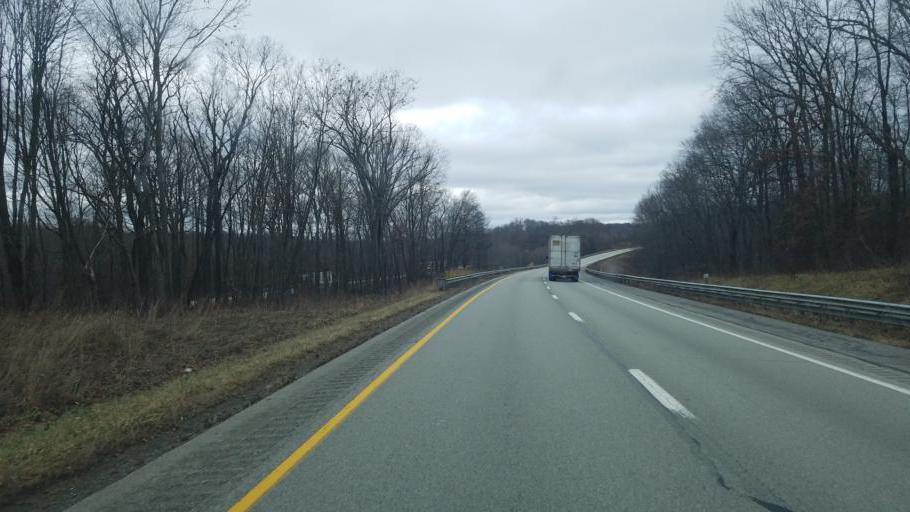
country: US
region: Pennsylvania
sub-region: Mercer County
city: Grove City
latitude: 41.2038
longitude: -79.9290
